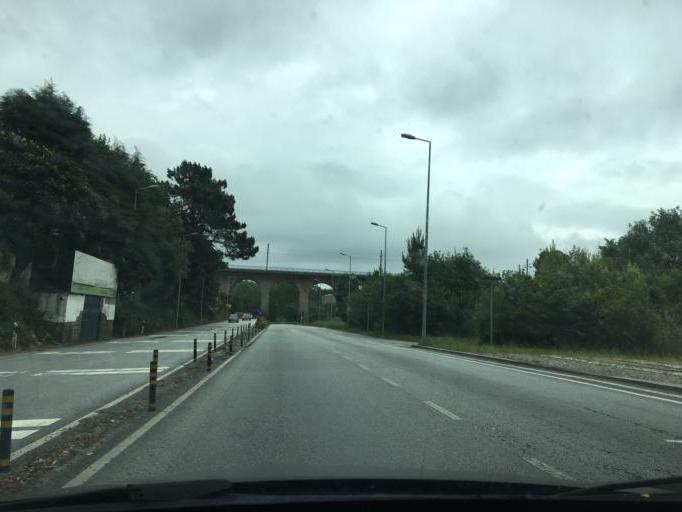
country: PT
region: Porto
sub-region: Maia
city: Maia
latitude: 41.2262
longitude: -8.6343
